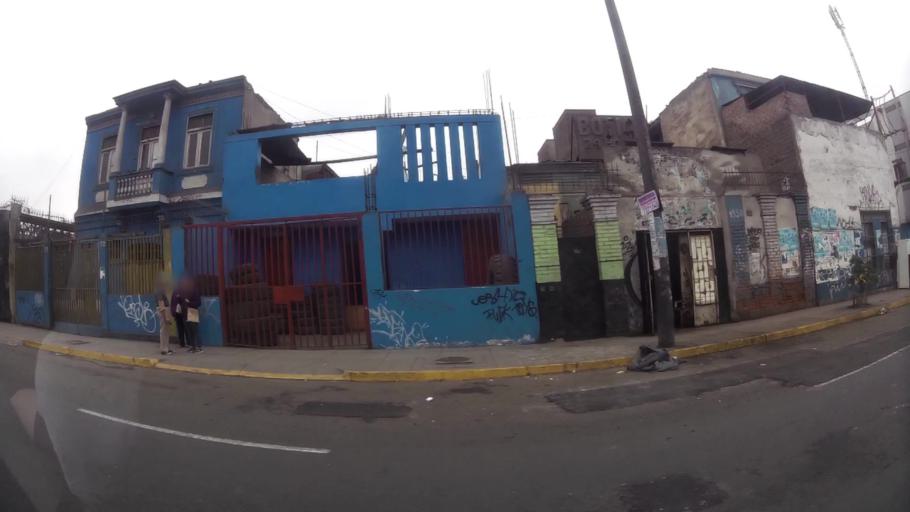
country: PE
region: Lima
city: Lima
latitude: -12.0574
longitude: -77.0162
